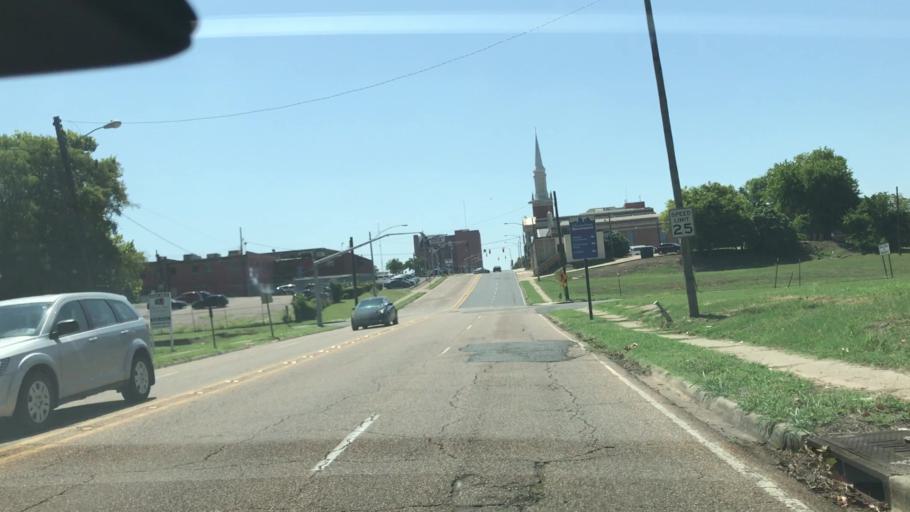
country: US
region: Louisiana
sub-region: Caddo Parish
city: Shreveport
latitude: 32.5130
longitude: -93.7548
